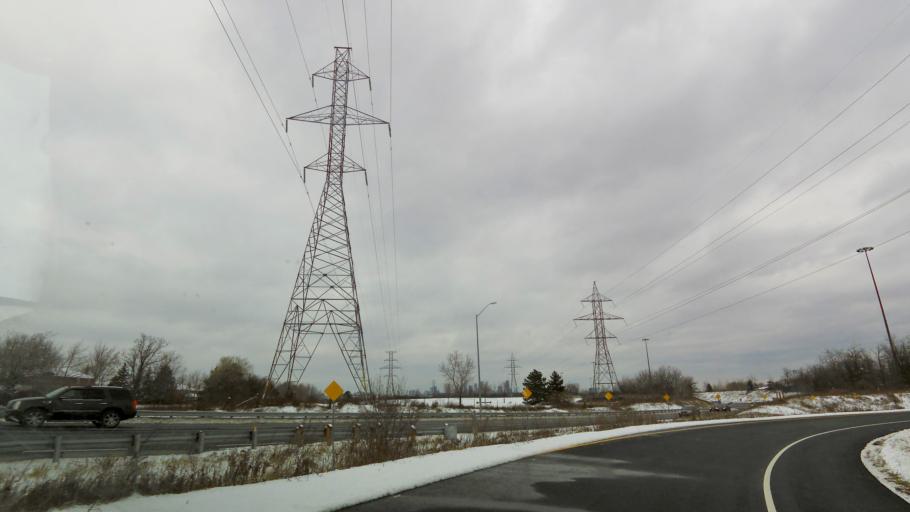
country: CA
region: Ontario
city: Mississauga
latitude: 43.5556
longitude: -79.6974
